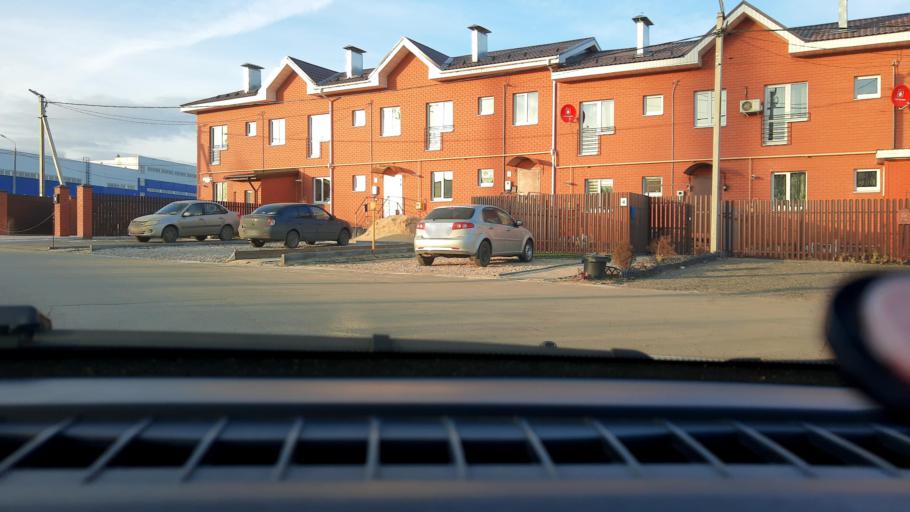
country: RU
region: Nizjnij Novgorod
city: Afonino
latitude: 56.2135
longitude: 44.0860
